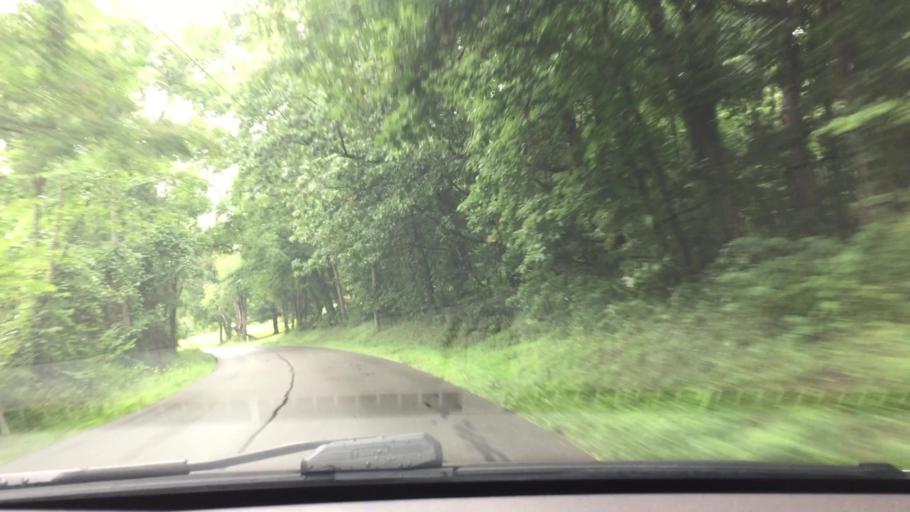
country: US
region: Pennsylvania
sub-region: Washington County
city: Muse
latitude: 40.2998
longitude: -80.1932
